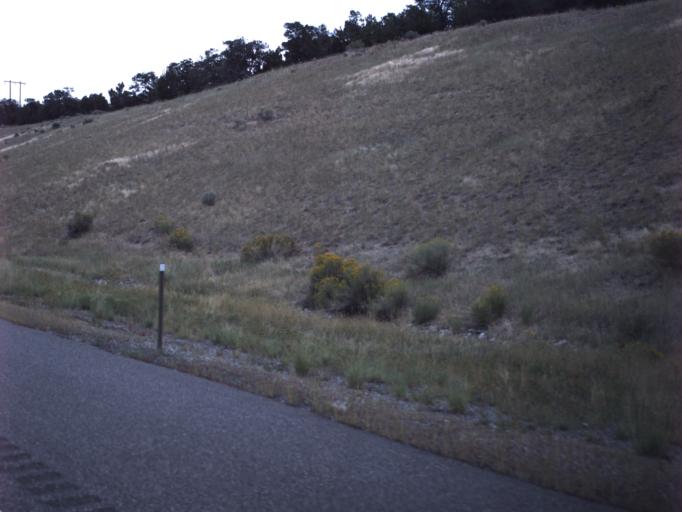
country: US
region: Utah
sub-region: Sevier County
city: Monroe
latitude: 38.5518
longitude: -112.3663
